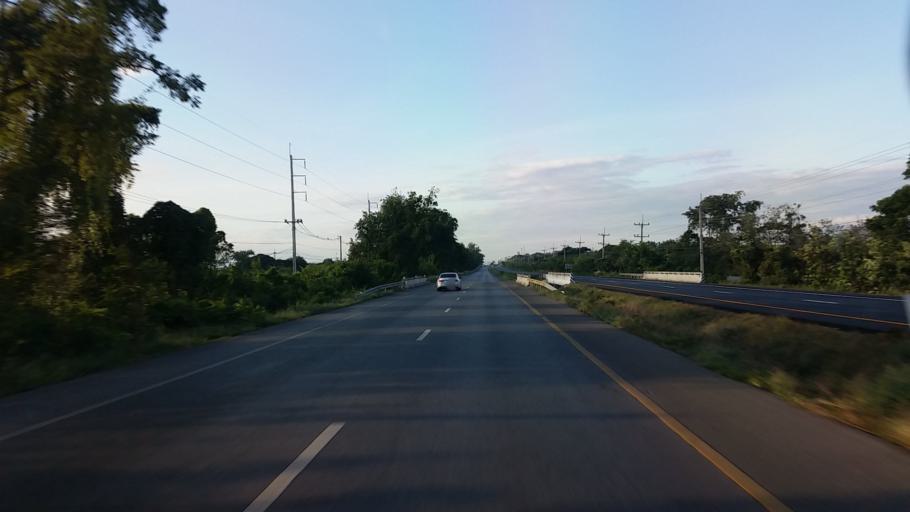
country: TH
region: Lop Buri
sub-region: Amphoe Tha Luang
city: Tha Luang
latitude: 15.1034
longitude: 101.0215
